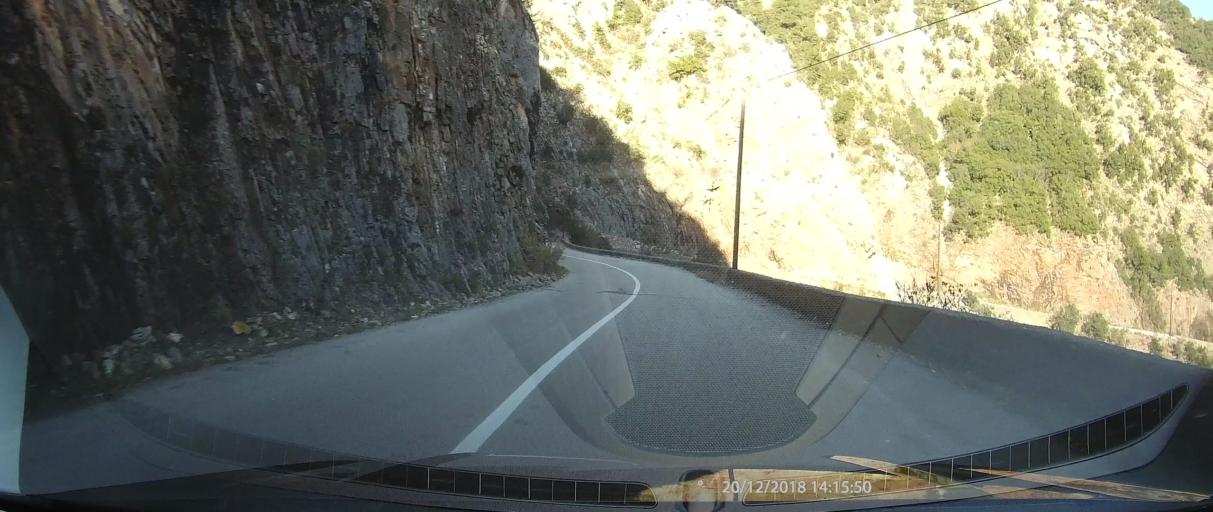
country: GR
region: West Greece
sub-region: Nomos Aitolias kai Akarnanias
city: Thermo
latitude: 38.7505
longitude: 21.6574
